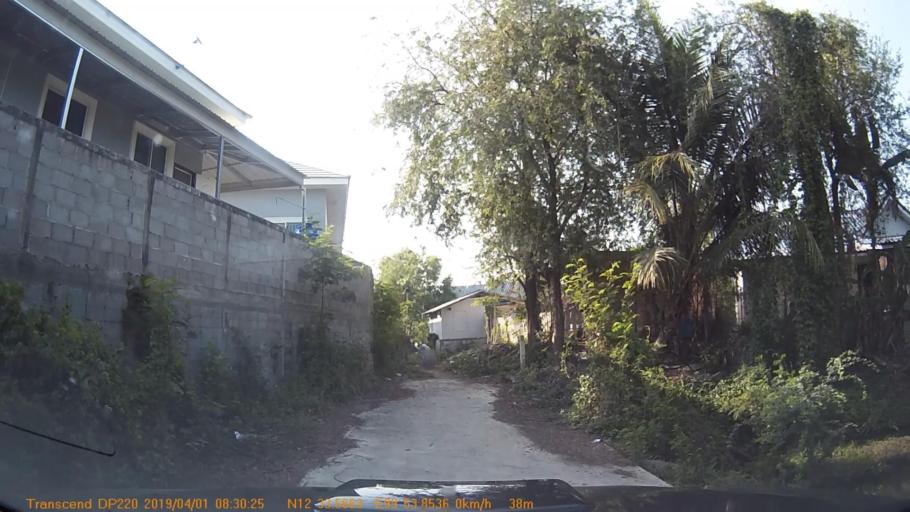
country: TH
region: Prachuap Khiri Khan
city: Hua Hin
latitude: 12.5596
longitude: 99.8975
